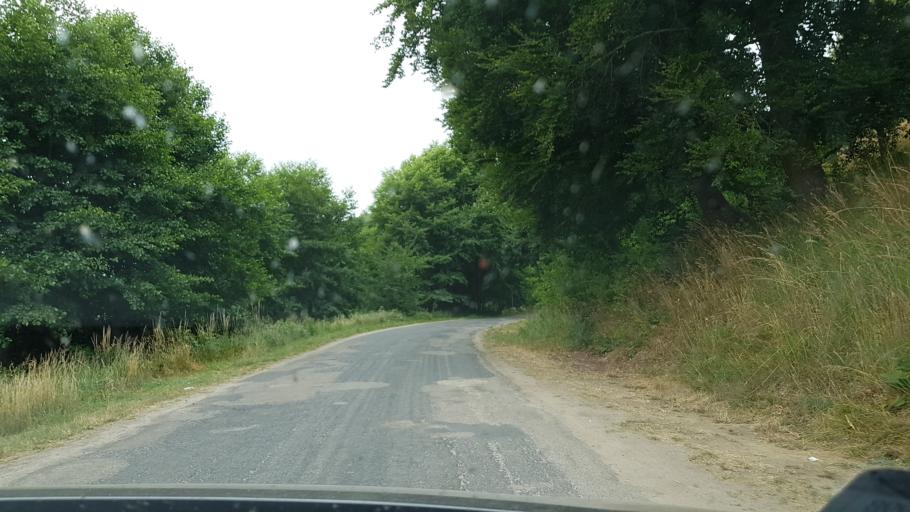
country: PL
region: West Pomeranian Voivodeship
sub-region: Powiat kamienski
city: Miedzyzdroje
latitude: 53.9613
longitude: 14.5705
